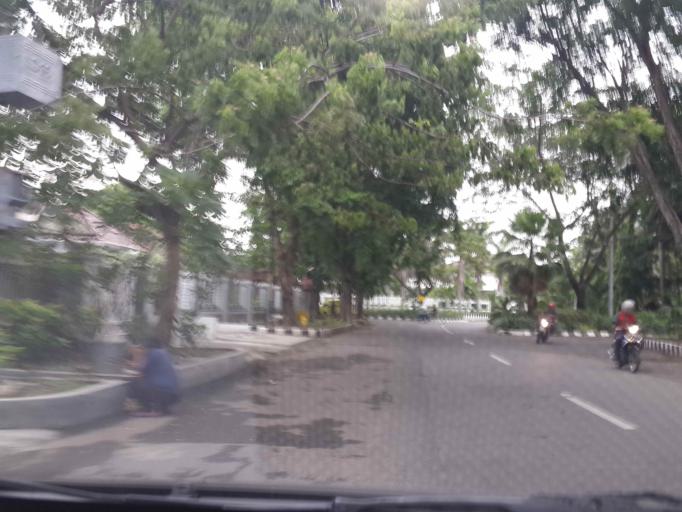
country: ID
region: East Java
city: Gubengairlangga
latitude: -7.2805
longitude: 112.7353
